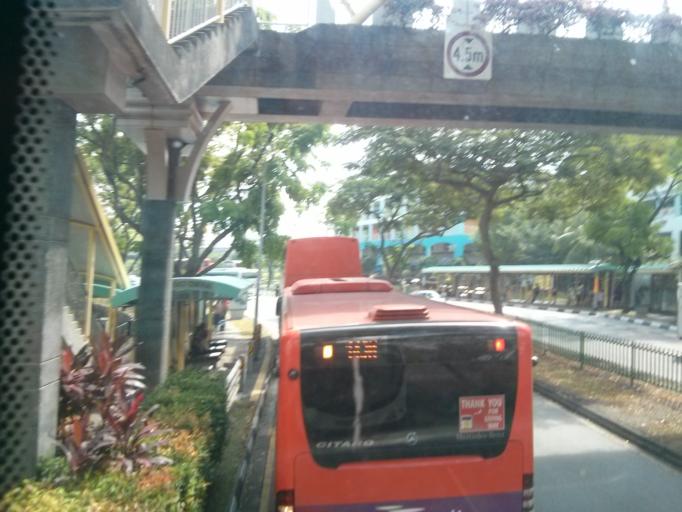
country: SG
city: Singapore
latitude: 1.3344
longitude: 103.7384
